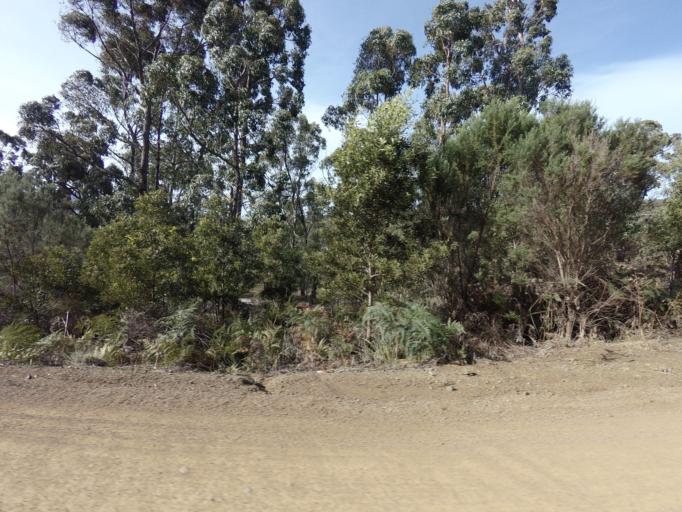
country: AU
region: Tasmania
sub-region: Kingborough
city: Kettering
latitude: -43.0836
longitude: 147.2647
